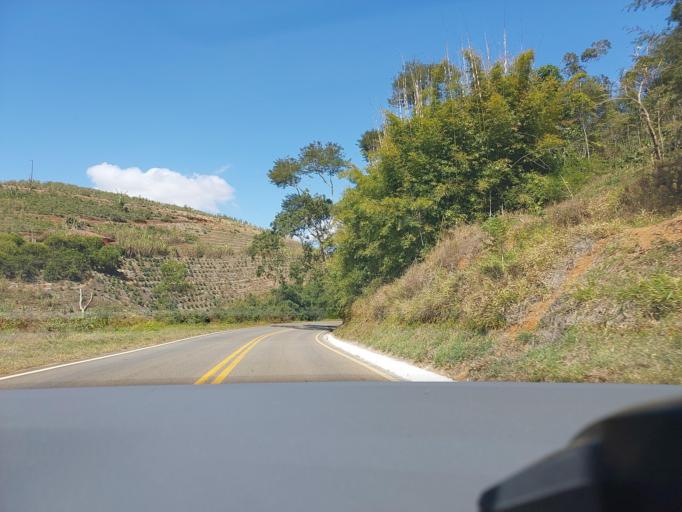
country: BR
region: Minas Gerais
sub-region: Mirai
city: Mirai
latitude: -21.0215
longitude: -42.5413
